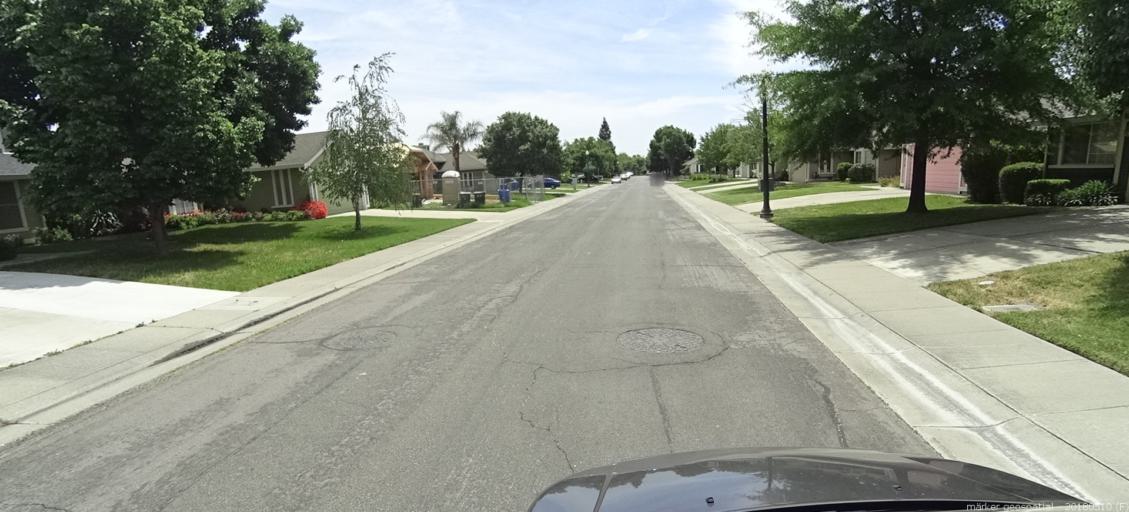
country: US
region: California
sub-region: Sacramento County
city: Rio Linda
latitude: 38.6584
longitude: -121.4636
